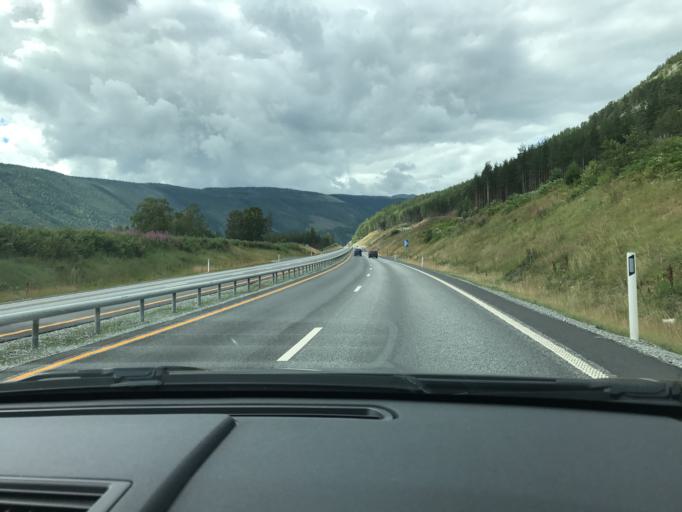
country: NO
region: Oppland
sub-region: Nord-Fron
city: Vinstra
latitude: 61.6650
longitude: 9.6393
